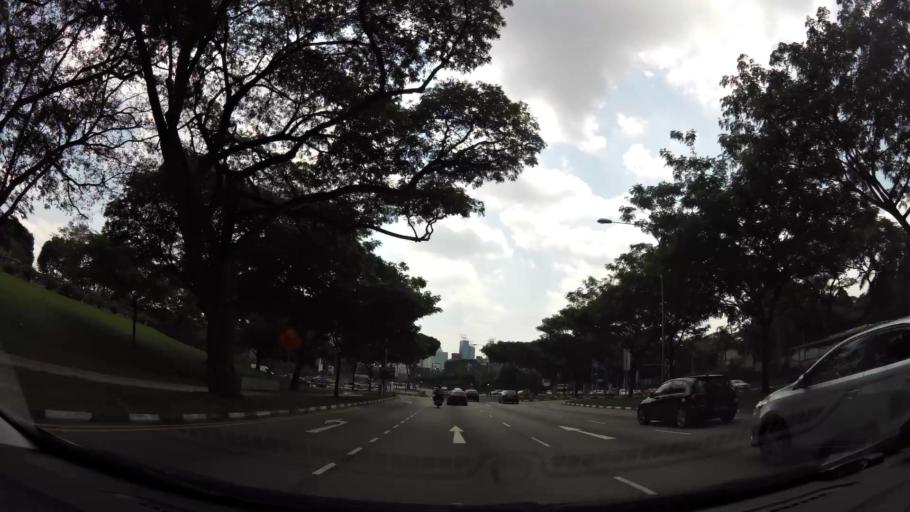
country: SG
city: Singapore
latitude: 1.3084
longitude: 103.8462
